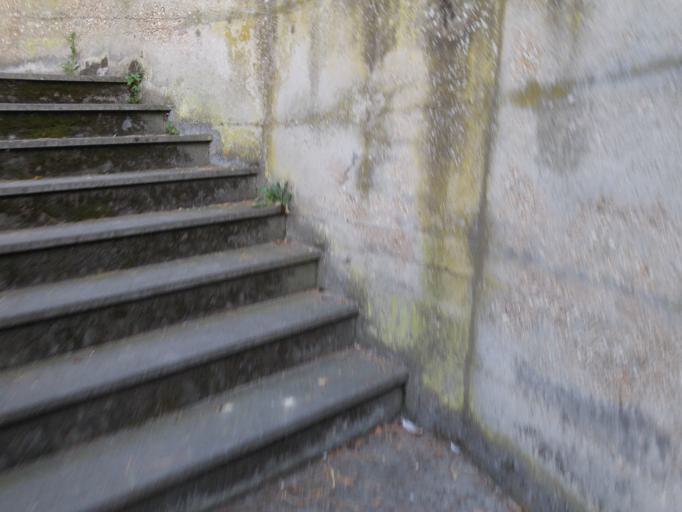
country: IT
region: Abruzzo
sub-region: Provincia di Teramo
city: Castilenti
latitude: 42.5335
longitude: 13.9185
